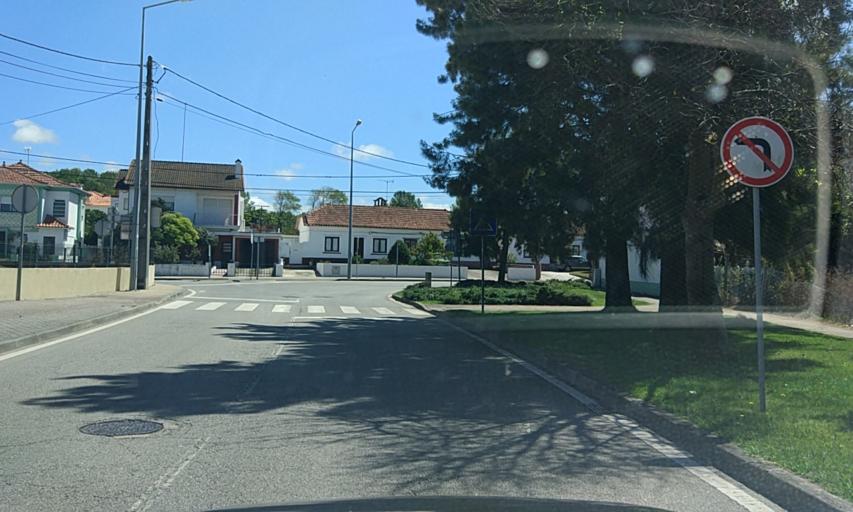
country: PT
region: Aveiro
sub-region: Ilhavo
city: Ilhavo
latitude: 40.5885
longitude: -8.6787
